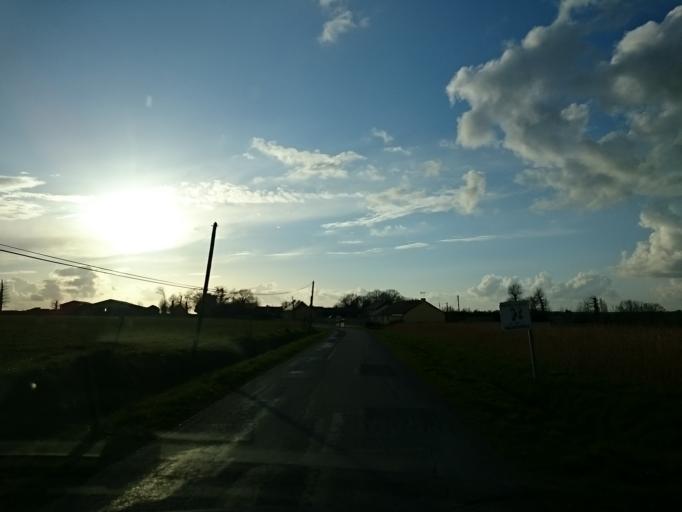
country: FR
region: Brittany
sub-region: Departement d'Ille-et-Vilaine
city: Crevin
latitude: 47.9198
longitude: -1.6416
